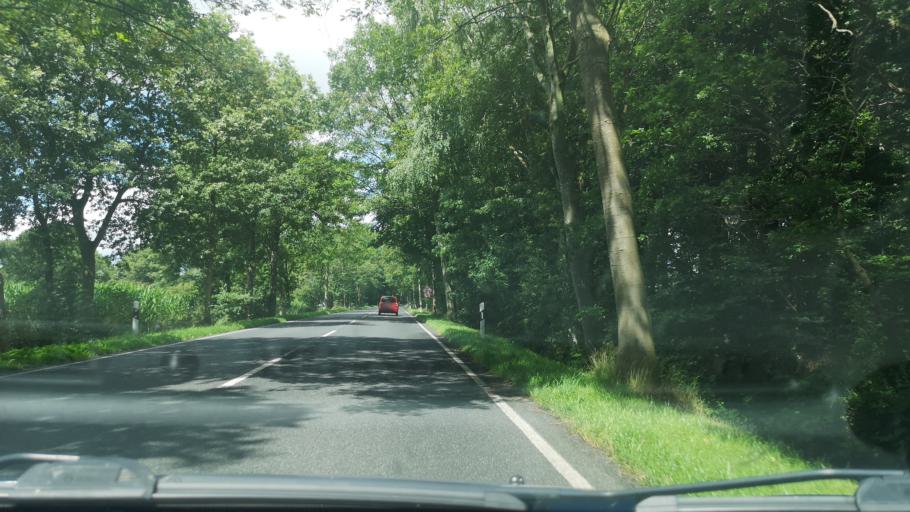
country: DE
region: Lower Saxony
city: Langen
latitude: 53.6378
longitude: 8.6185
